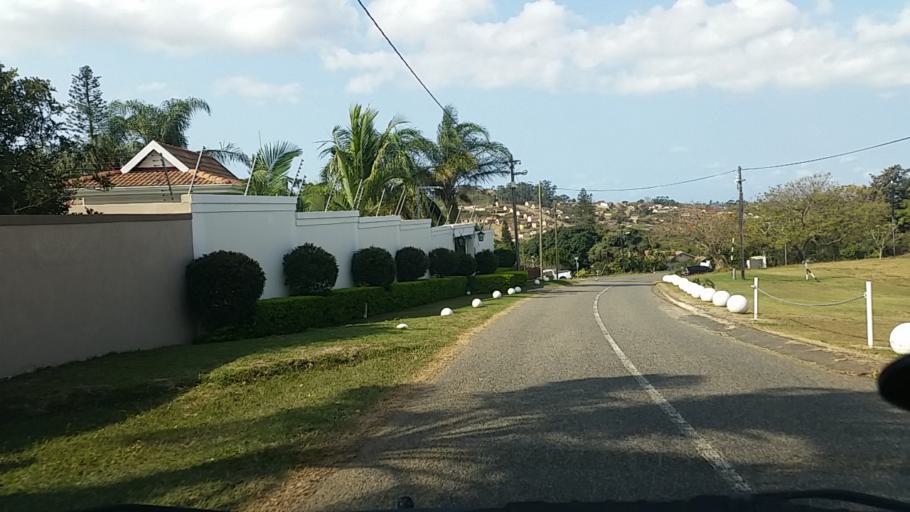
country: ZA
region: KwaZulu-Natal
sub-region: eThekwini Metropolitan Municipality
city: Berea
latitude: -29.8319
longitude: 30.9555
